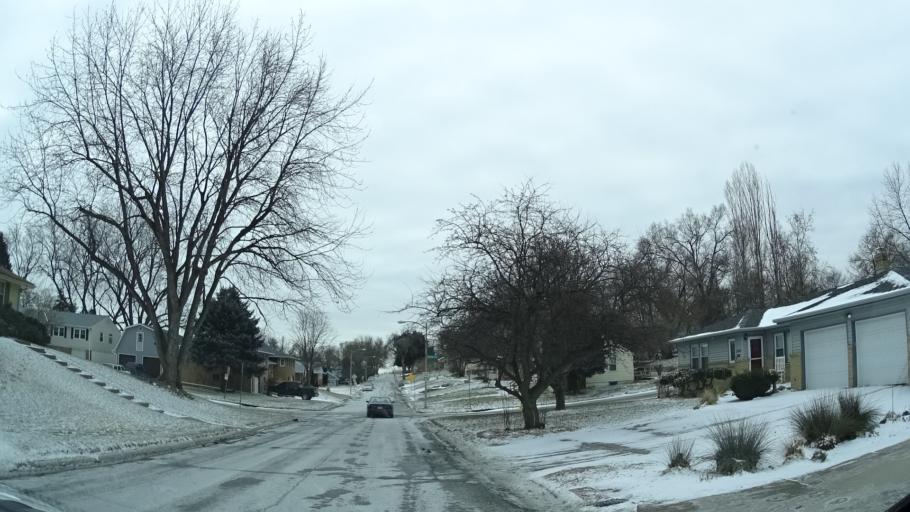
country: US
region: Nebraska
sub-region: Douglas County
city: Omaha
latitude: 41.2736
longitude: -96.0049
